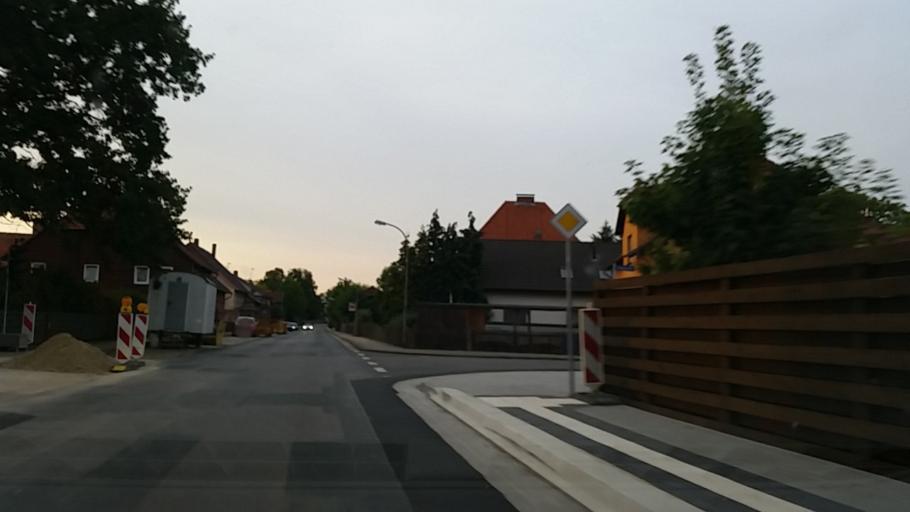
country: DE
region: Lower Saxony
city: Vordorf
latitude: 52.3651
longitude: 10.5232
